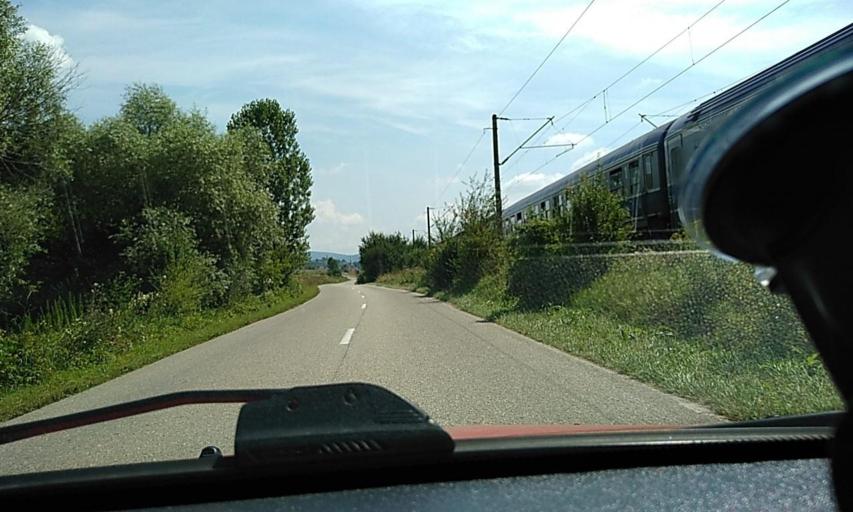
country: RO
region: Brasov
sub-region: Comuna Hoghiz
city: Hoghiz
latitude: 46.0293
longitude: 25.3771
